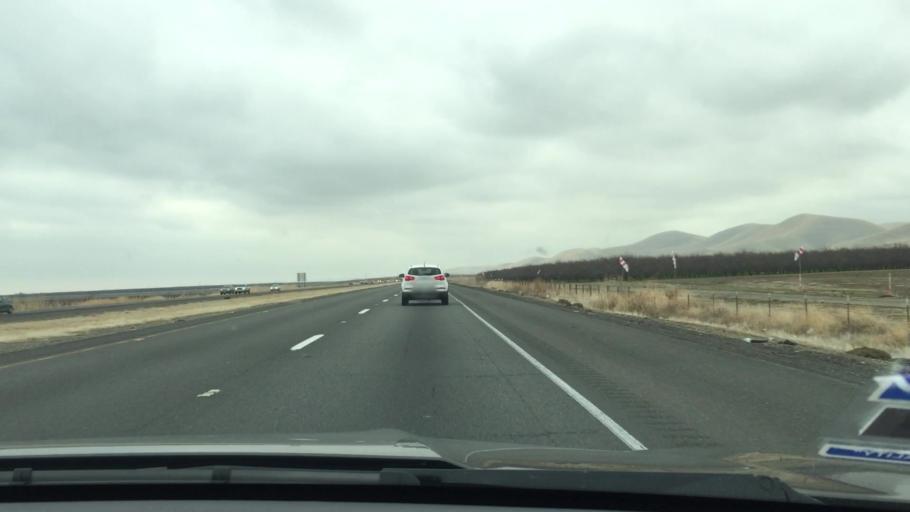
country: US
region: California
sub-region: Merced County
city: Gustine
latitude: 37.2322
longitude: -121.0856
